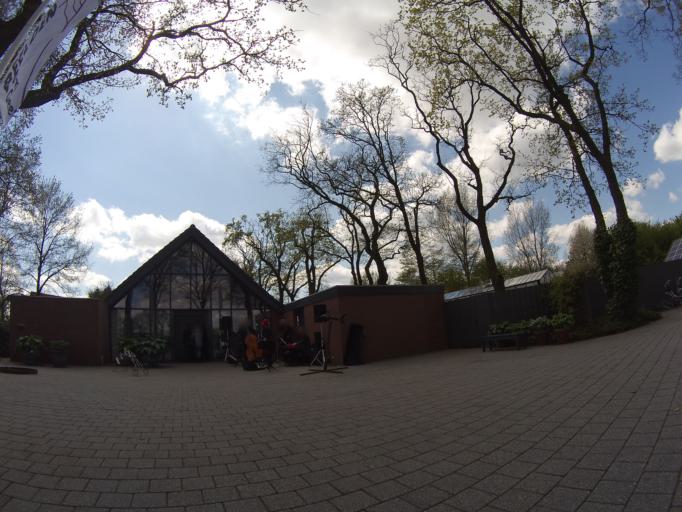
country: NL
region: Drenthe
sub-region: Gemeente Coevorden
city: Dalen
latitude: 52.7401
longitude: 6.7039
